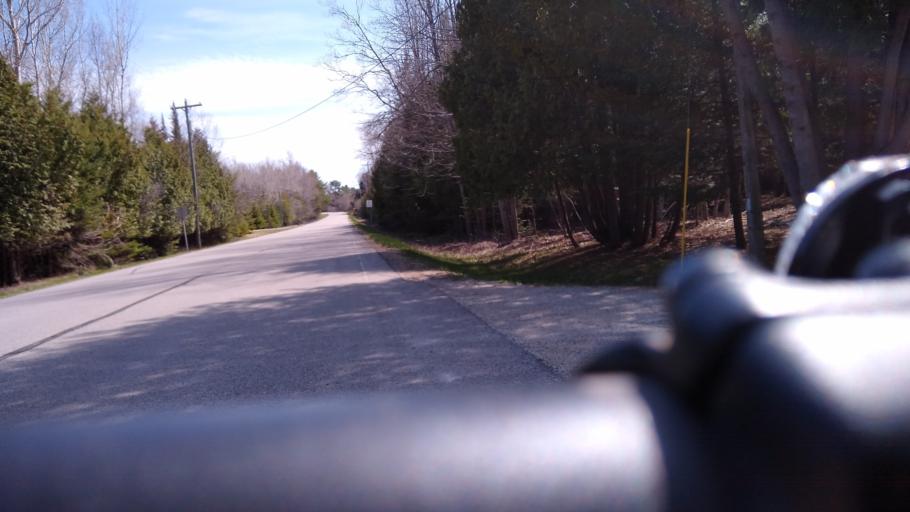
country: US
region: Michigan
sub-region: Delta County
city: Escanaba
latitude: 45.6916
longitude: -87.1526
